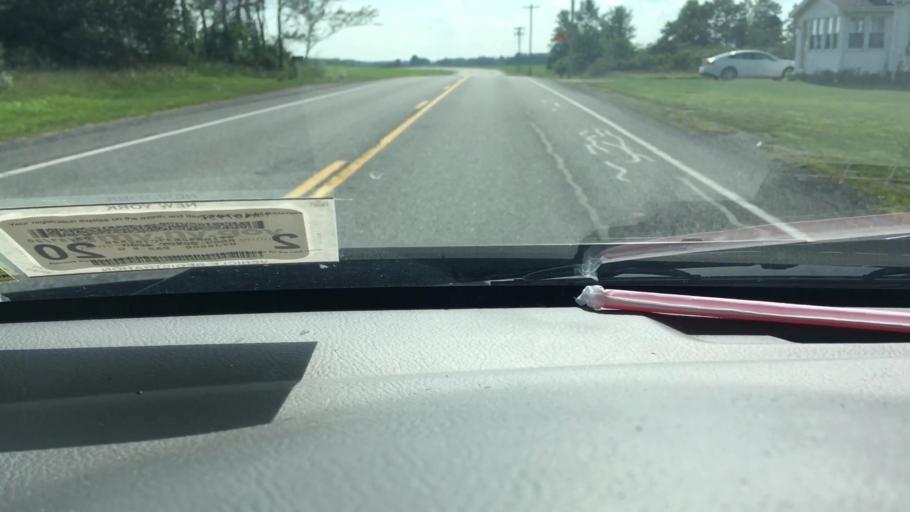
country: US
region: New York
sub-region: Genesee County
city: Batavia
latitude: 43.0350
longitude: -78.1505
